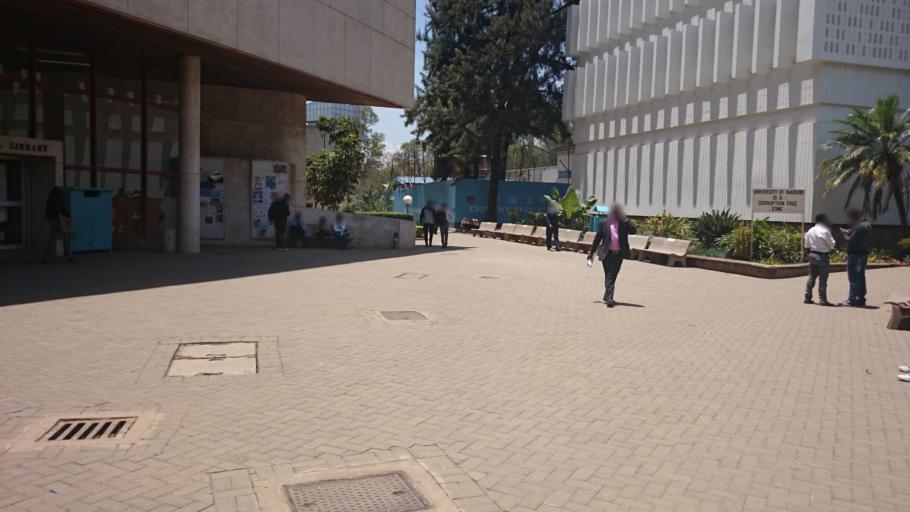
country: KE
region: Nairobi Area
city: Nairobi
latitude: -1.2802
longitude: 36.8163
